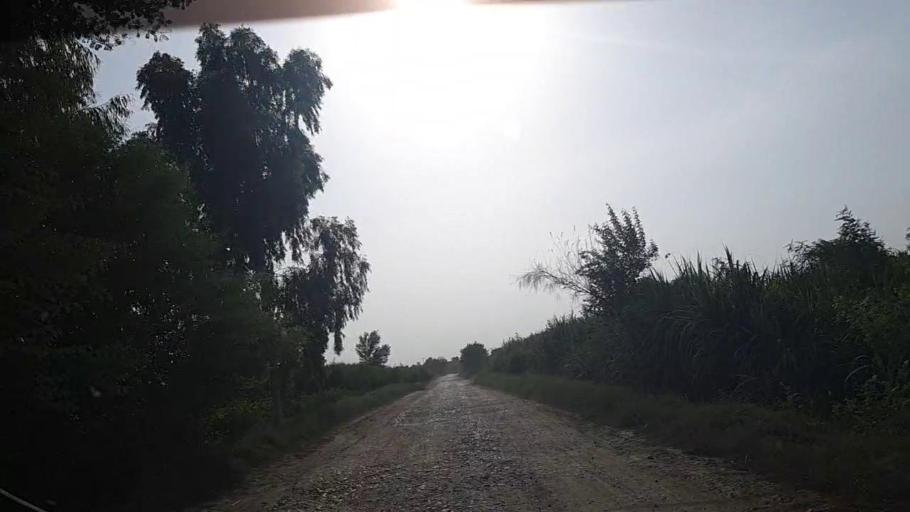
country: PK
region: Sindh
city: Ghotki
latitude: 28.0167
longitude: 69.2902
